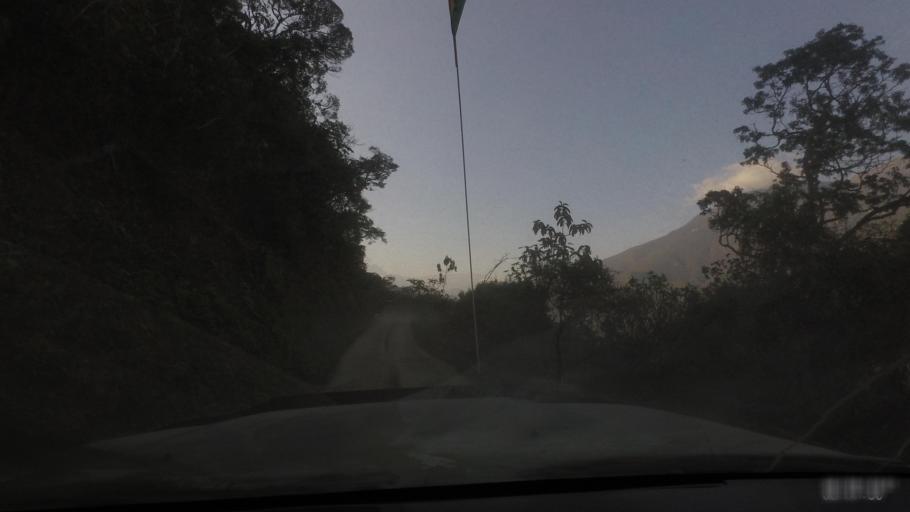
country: BO
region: La Paz
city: Quime
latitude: -16.5220
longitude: -66.7699
